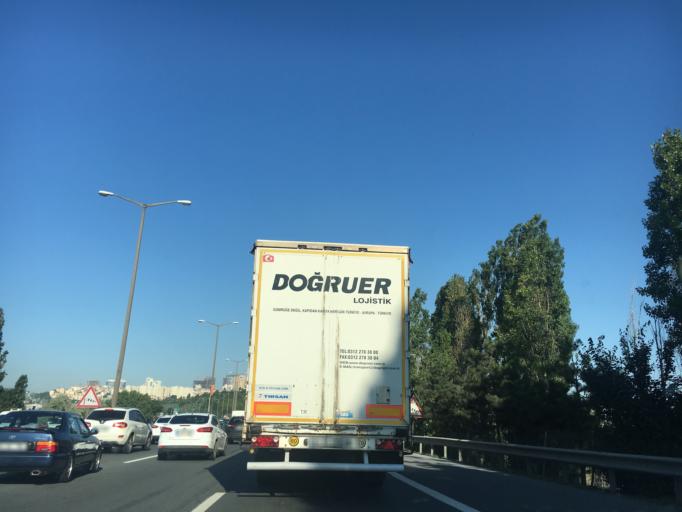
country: TR
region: Istanbul
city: Esenyurt
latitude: 41.0590
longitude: 28.7036
